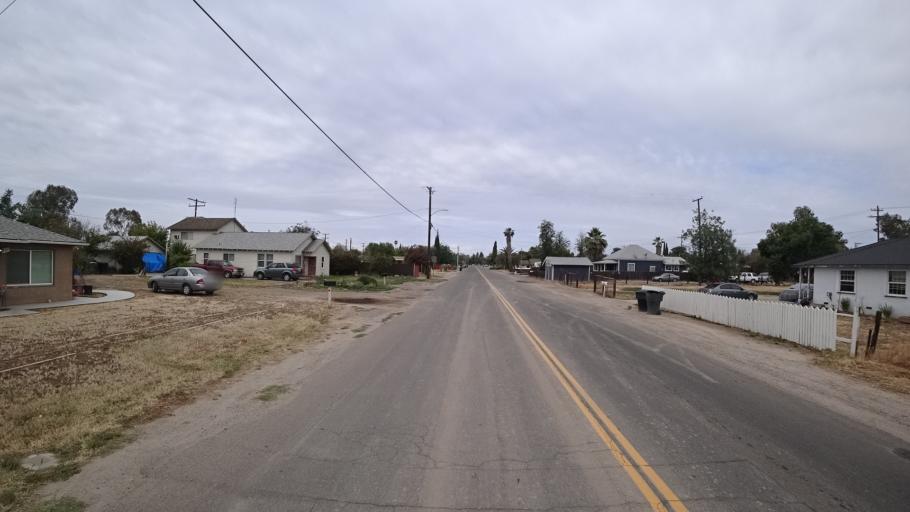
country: US
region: California
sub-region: Kings County
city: Hanford
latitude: 36.3240
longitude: -119.6590
